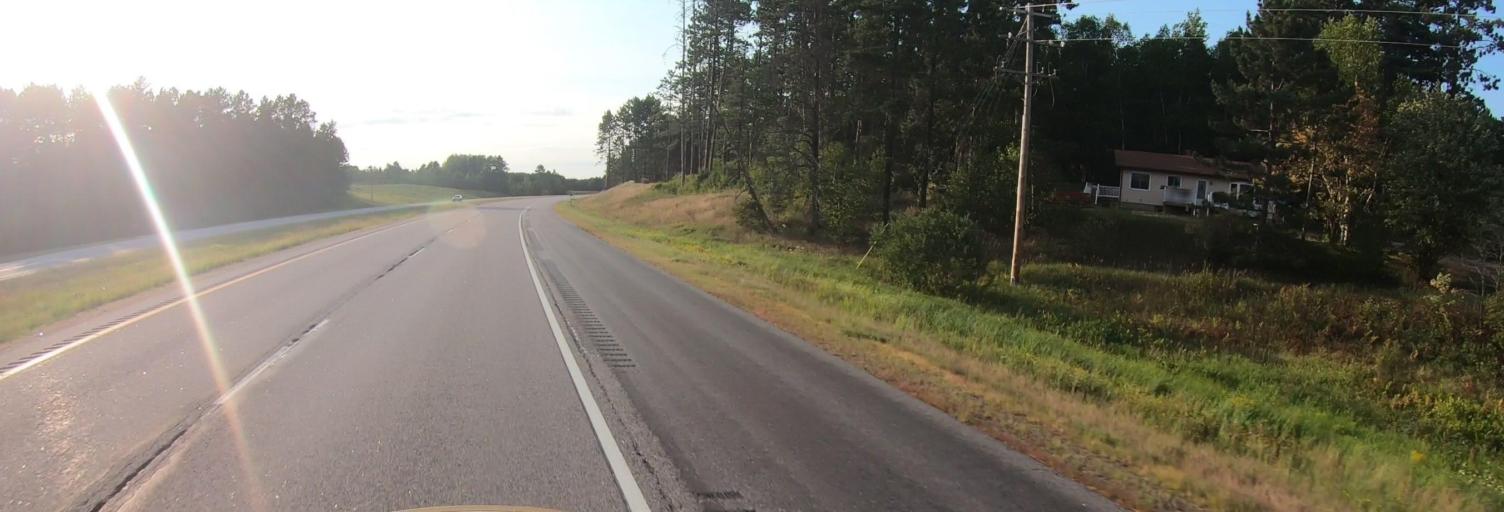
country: US
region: Minnesota
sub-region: Saint Louis County
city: Mountain Iron
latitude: 47.6712
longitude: -92.6317
